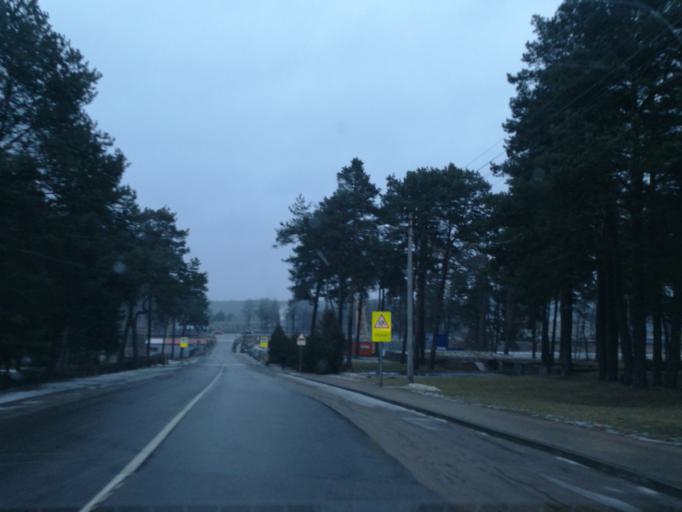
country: LT
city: Grigiskes
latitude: 54.6740
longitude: 25.0812
